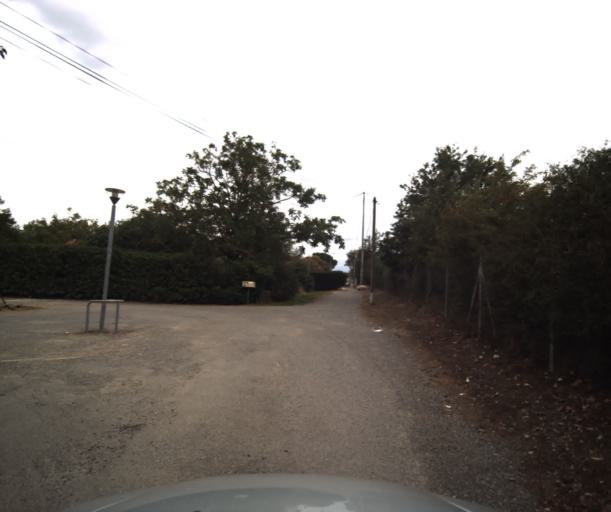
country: FR
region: Midi-Pyrenees
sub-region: Departement de la Haute-Garonne
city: Muret
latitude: 43.4497
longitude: 1.3129
